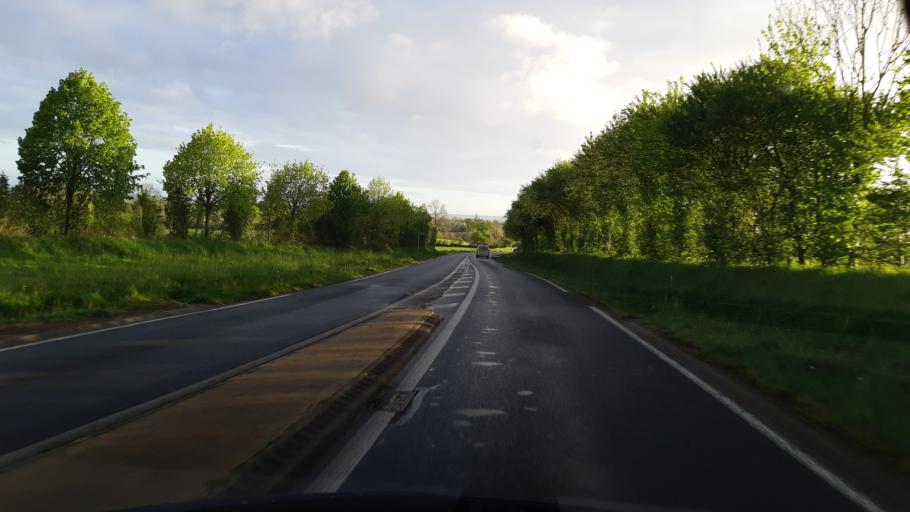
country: FR
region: Lower Normandy
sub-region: Departement de la Manche
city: Agneaux
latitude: 49.0322
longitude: -1.1356
